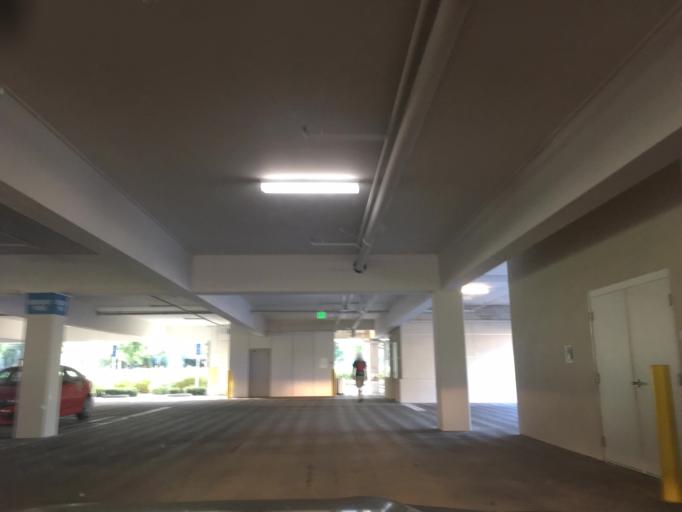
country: US
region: California
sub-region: Santa Clara County
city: Sunnyvale
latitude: 37.3917
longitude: -122.0332
